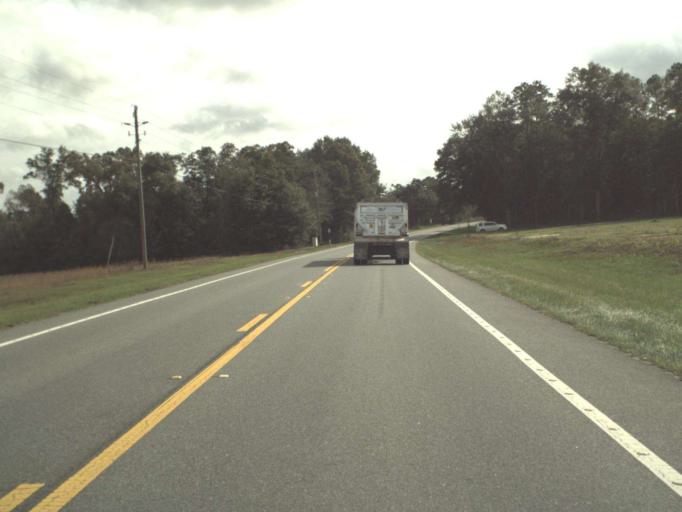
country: US
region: Alabama
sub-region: Escambia County
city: East Brewton
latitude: 30.9374
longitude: -87.0252
